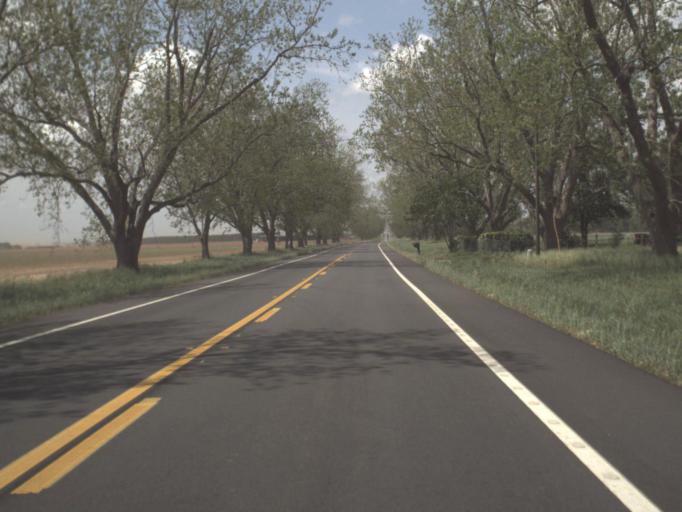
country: US
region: Florida
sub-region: Escambia County
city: Century
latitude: 30.8664
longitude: -87.1566
